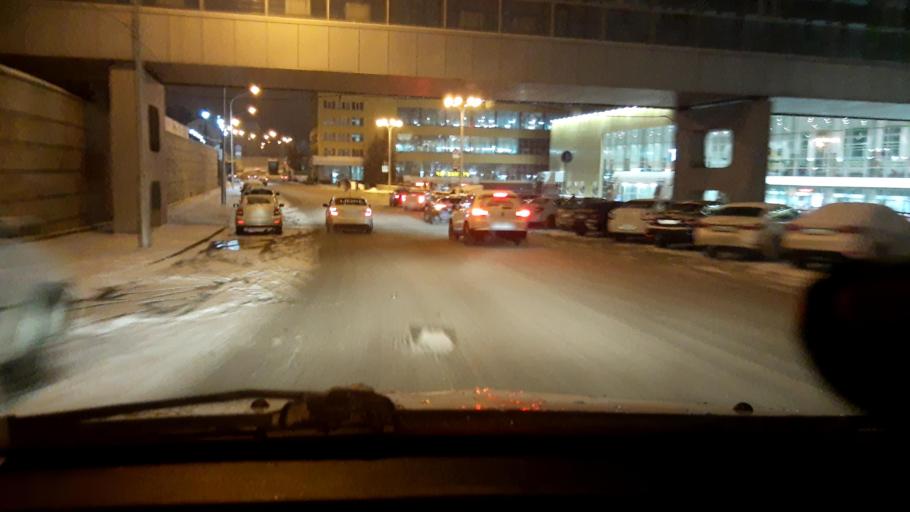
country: RU
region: Bashkortostan
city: Ufa
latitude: 54.7486
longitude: 55.9503
